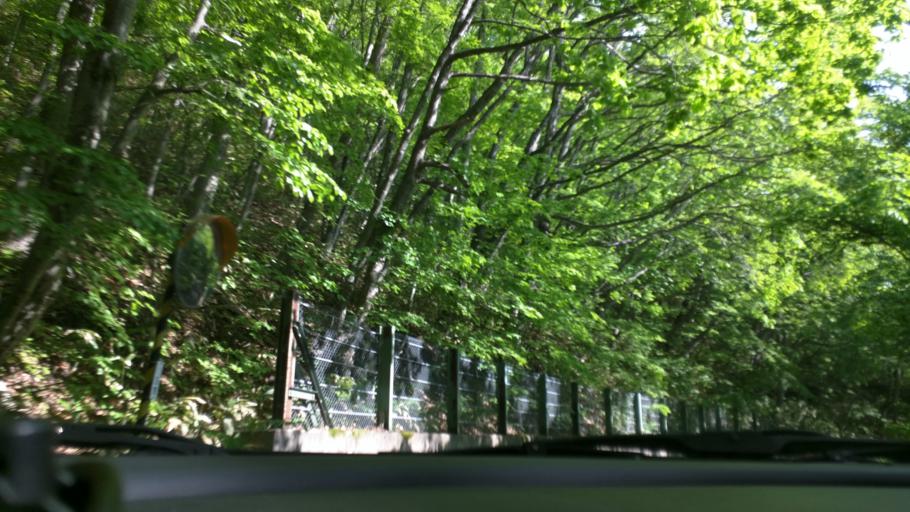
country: JP
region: Tochigi
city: Kuroiso
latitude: 37.2664
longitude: 140.0780
